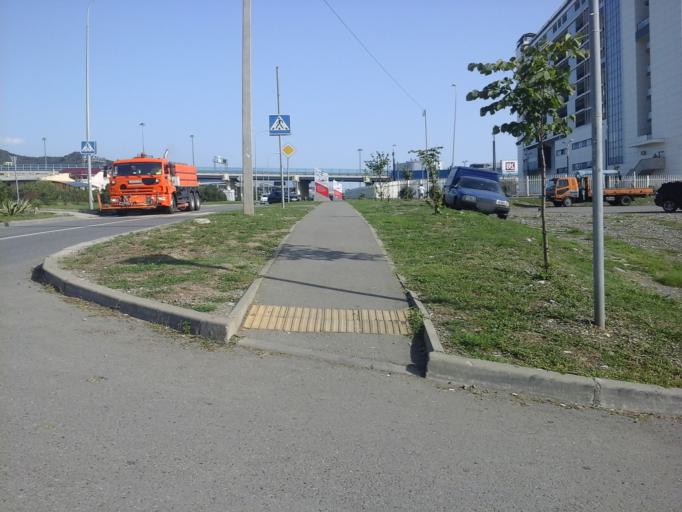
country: RU
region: Krasnodarskiy
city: Adler
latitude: 43.4141
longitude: 39.9653
